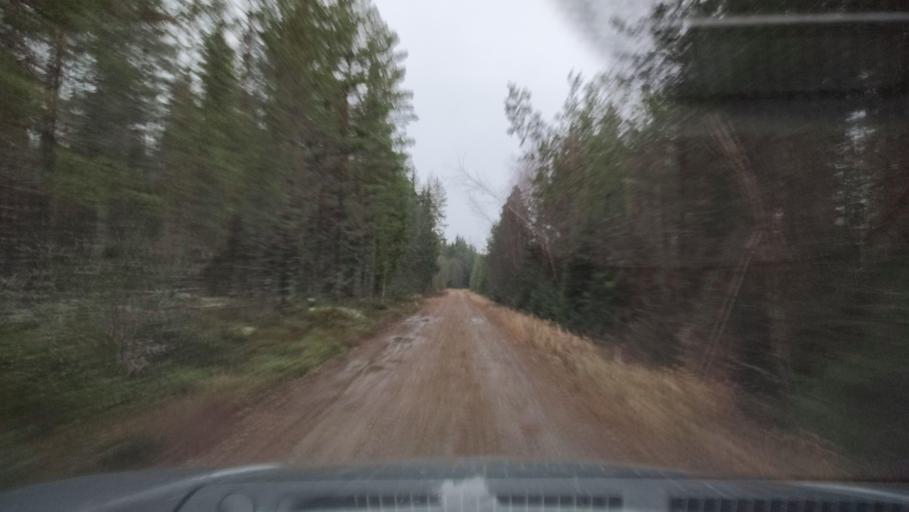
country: FI
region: Southern Ostrobothnia
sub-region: Suupohja
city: Karijoki
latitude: 62.1556
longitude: 21.5899
